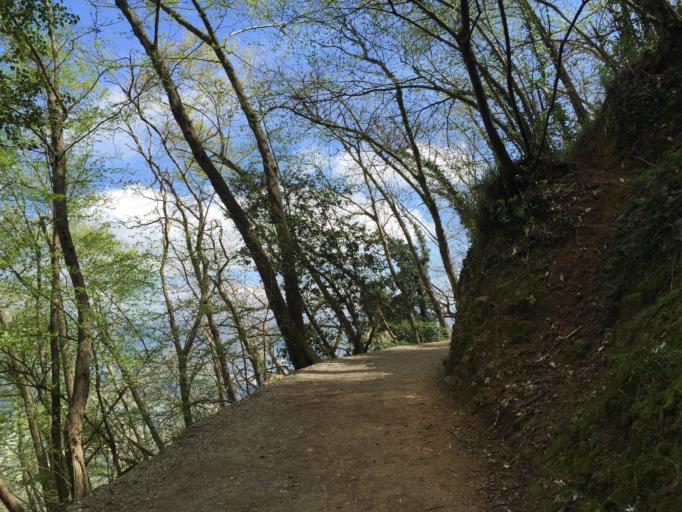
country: IT
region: Liguria
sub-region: Provincia di Genova
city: Camogli
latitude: 44.3269
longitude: 9.1745
